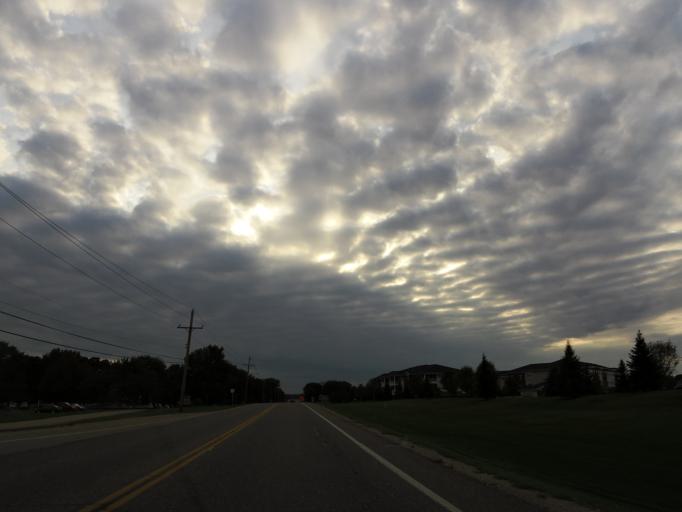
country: US
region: Minnesota
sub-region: Dakota County
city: Lakeville
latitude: 44.6561
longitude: -93.2334
